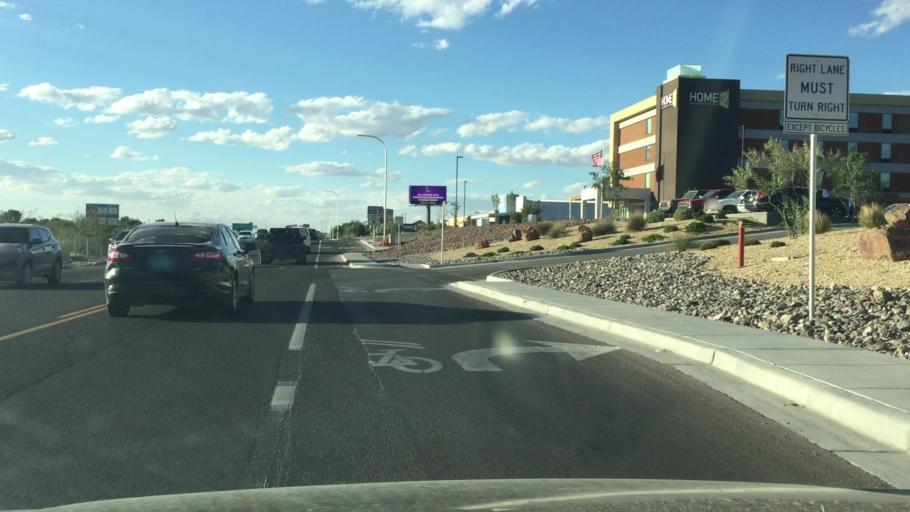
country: US
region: New Mexico
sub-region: Dona Ana County
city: Las Cruces
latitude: 32.3352
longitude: -106.7600
